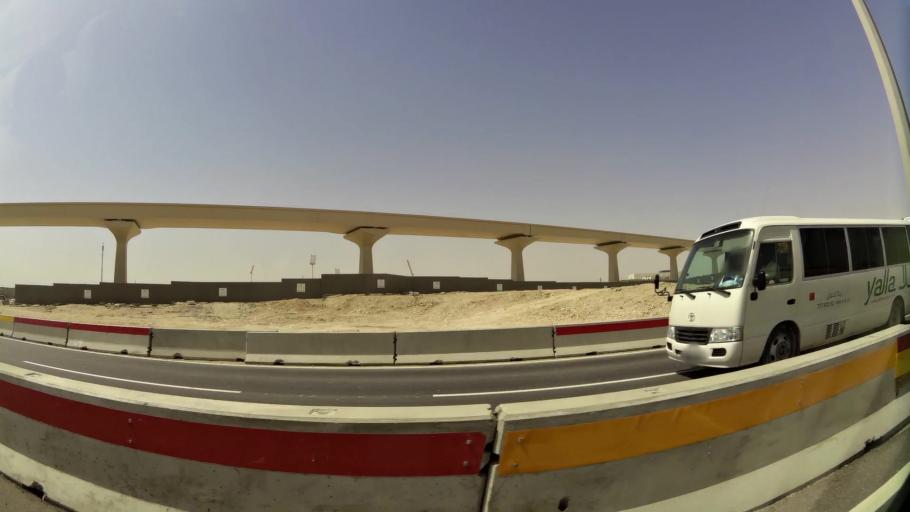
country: QA
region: Baladiyat Umm Salal
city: Umm Salal Muhammad
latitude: 25.3792
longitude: 51.4987
